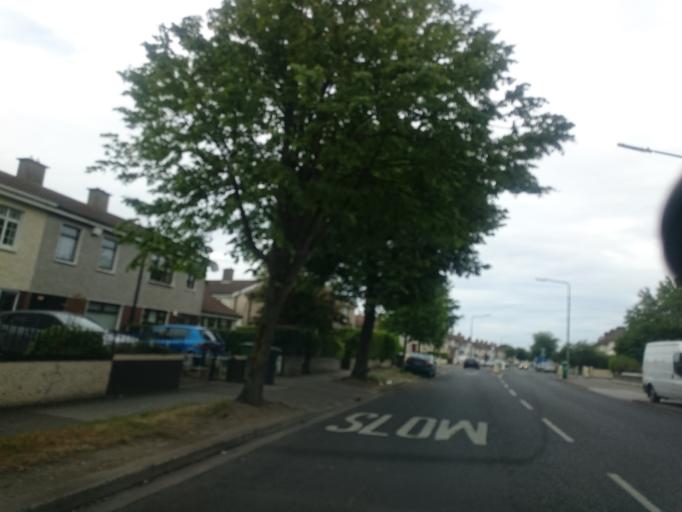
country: IE
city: Greenhills
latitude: 53.3164
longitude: -6.3072
